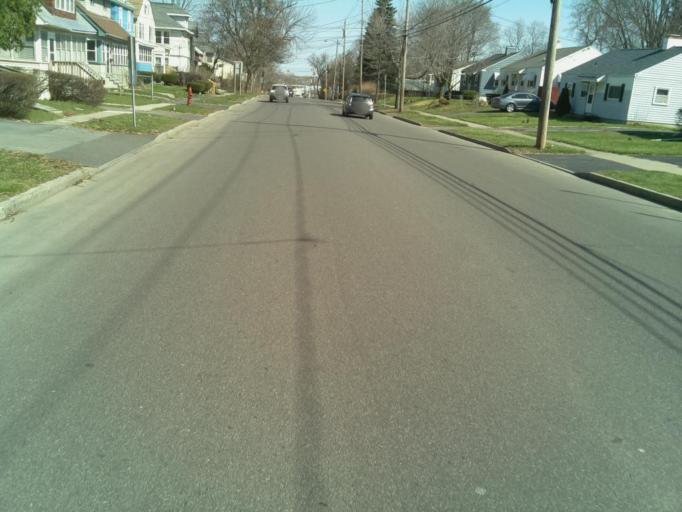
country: US
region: New York
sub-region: Onondaga County
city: Lyncourt
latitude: 43.0724
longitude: -76.1055
